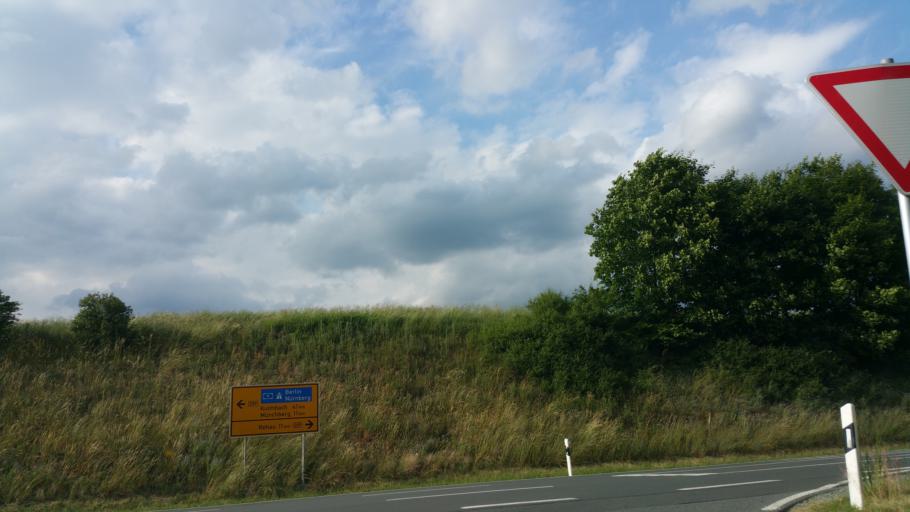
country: DE
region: Bavaria
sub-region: Upper Franconia
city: Schwarzenbach an der Saale
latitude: 50.2241
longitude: 11.9150
